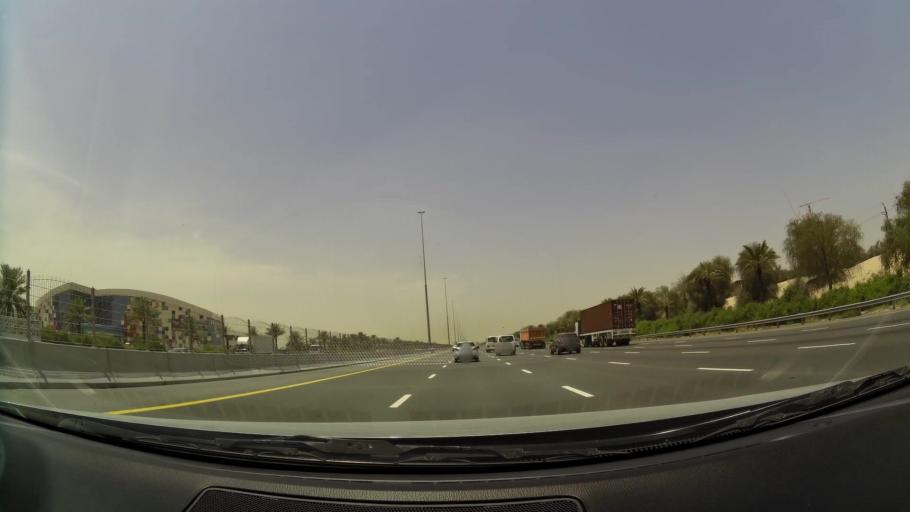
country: AE
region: Dubai
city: Dubai
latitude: 25.0859
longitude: 55.3176
